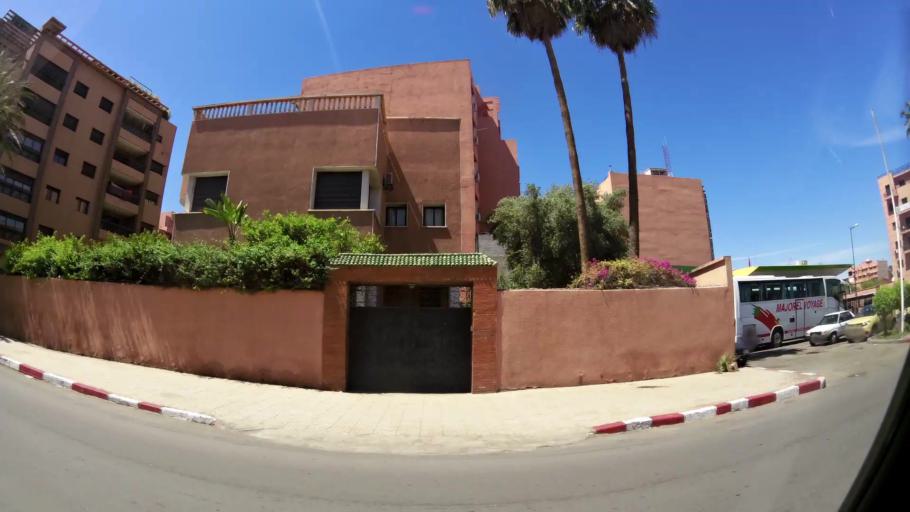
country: MA
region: Marrakech-Tensift-Al Haouz
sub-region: Marrakech
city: Marrakesh
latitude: 31.6330
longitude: -8.0037
